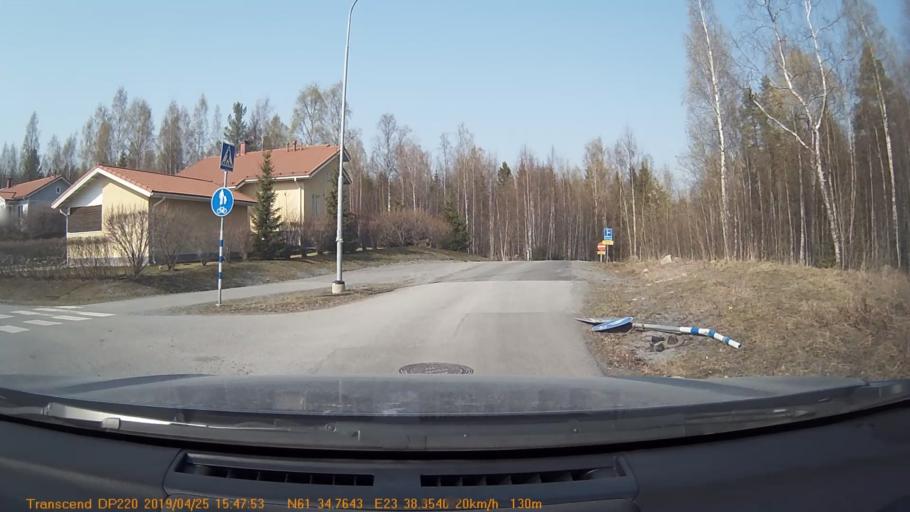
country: FI
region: Pirkanmaa
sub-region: Tampere
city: Yloejaervi
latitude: 61.5794
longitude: 23.6393
